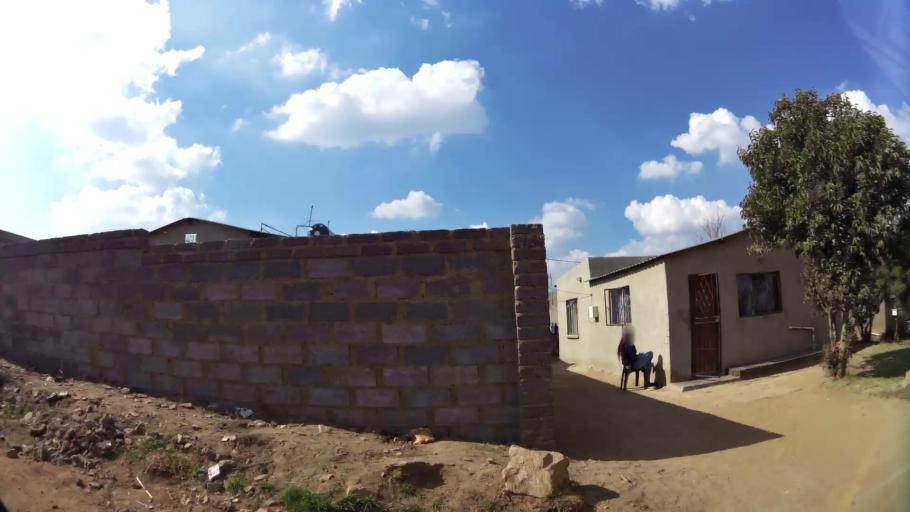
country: ZA
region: Gauteng
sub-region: City of Johannesburg Metropolitan Municipality
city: Roodepoort
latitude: -26.1953
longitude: 27.8708
